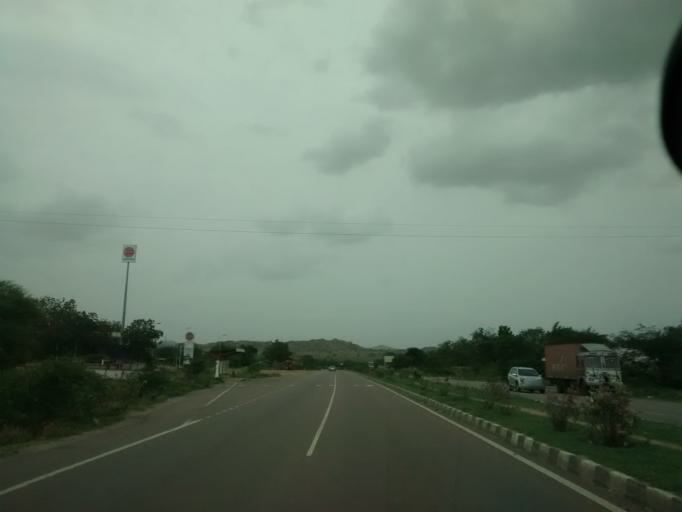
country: IN
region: Andhra Pradesh
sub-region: Kurnool
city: Ramapuram
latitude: 15.1697
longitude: 77.6814
